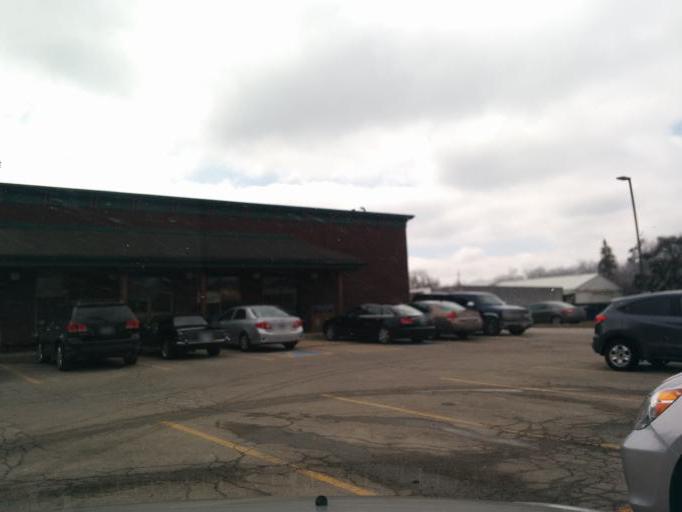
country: CA
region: Ontario
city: Waterloo
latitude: 43.5321
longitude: -80.5552
